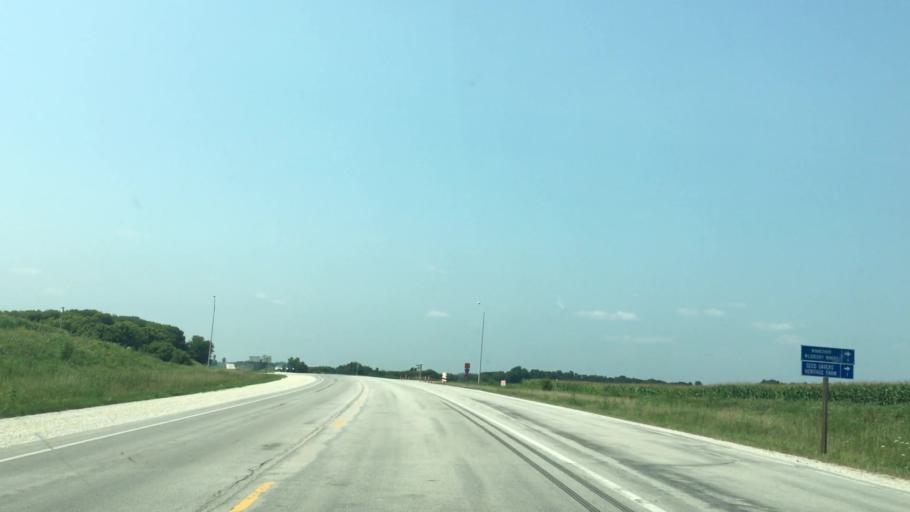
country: US
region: Iowa
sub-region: Winneshiek County
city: Decorah
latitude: 43.3665
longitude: -91.8055
